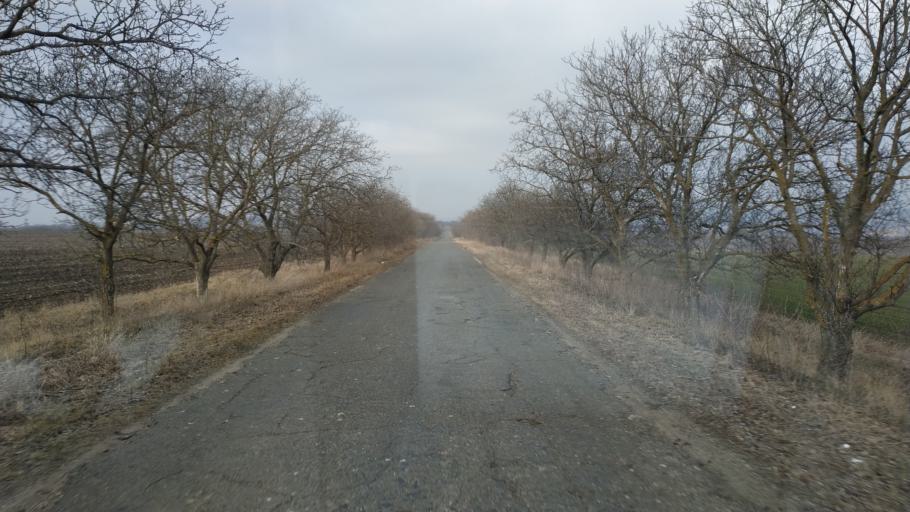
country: MD
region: Hincesti
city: Dancu
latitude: 46.8941
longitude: 28.3030
